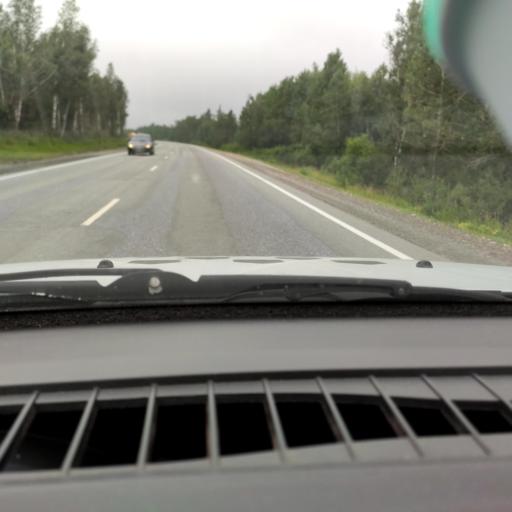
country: RU
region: Chelyabinsk
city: Zlatoust
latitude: 55.0299
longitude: 59.7225
